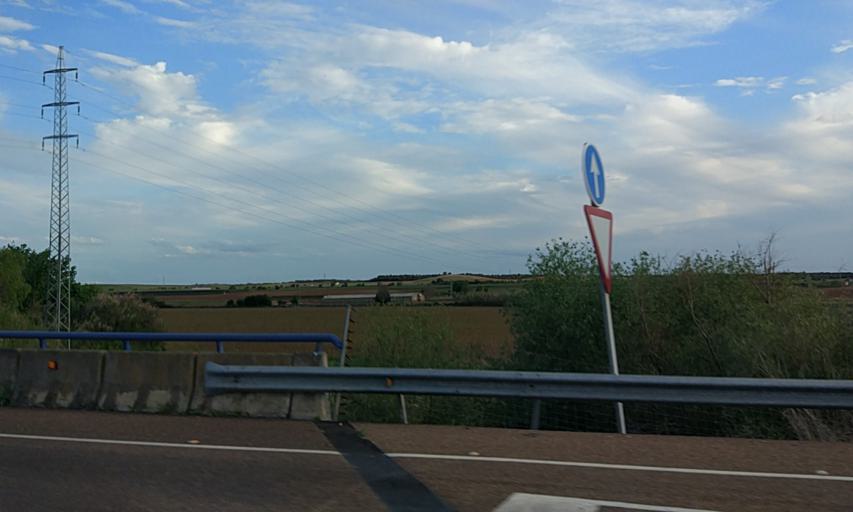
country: ES
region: Extremadura
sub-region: Provincia de Badajoz
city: Valdelacalzada
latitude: 38.8503
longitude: -6.6884
